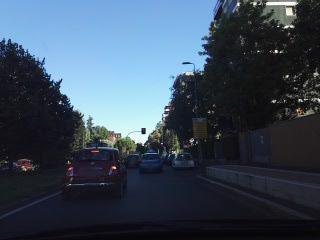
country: IT
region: Lombardy
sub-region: Citta metropolitana di Milano
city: Romano Banco
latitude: 45.4564
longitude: 9.1396
